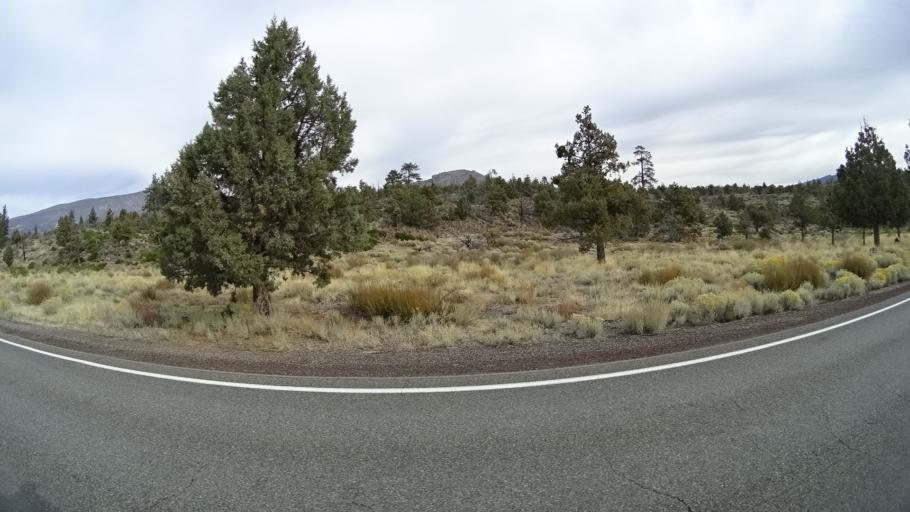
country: US
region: California
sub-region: Siskiyou County
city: Weed
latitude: 41.5614
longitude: -122.2604
